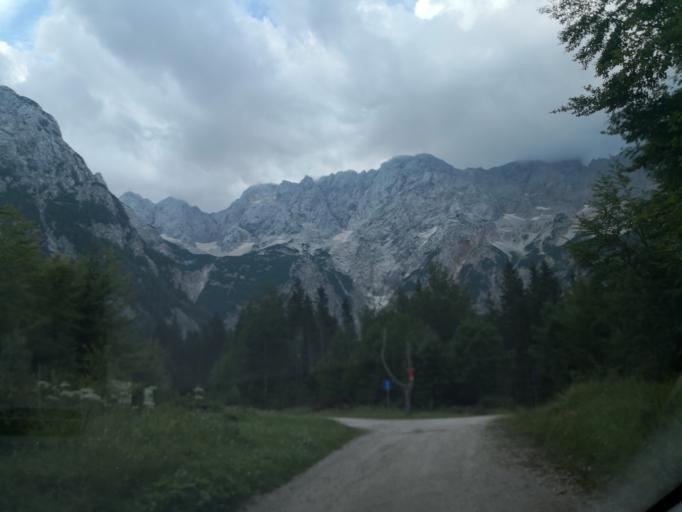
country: SI
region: Jezersko
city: Zgornje Jezersko
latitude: 46.3884
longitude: 14.5357
